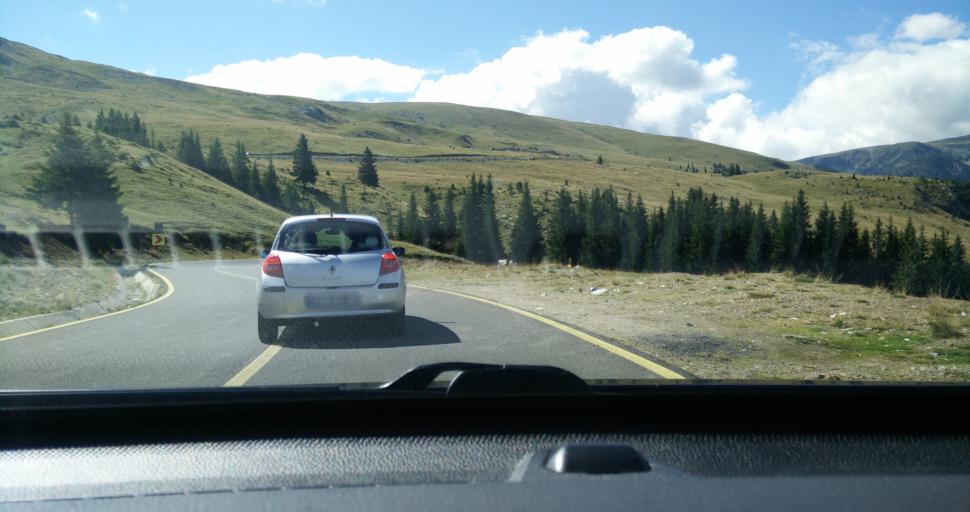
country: RO
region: Gorj
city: Novaci-Straini
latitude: 45.3902
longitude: 23.6410
